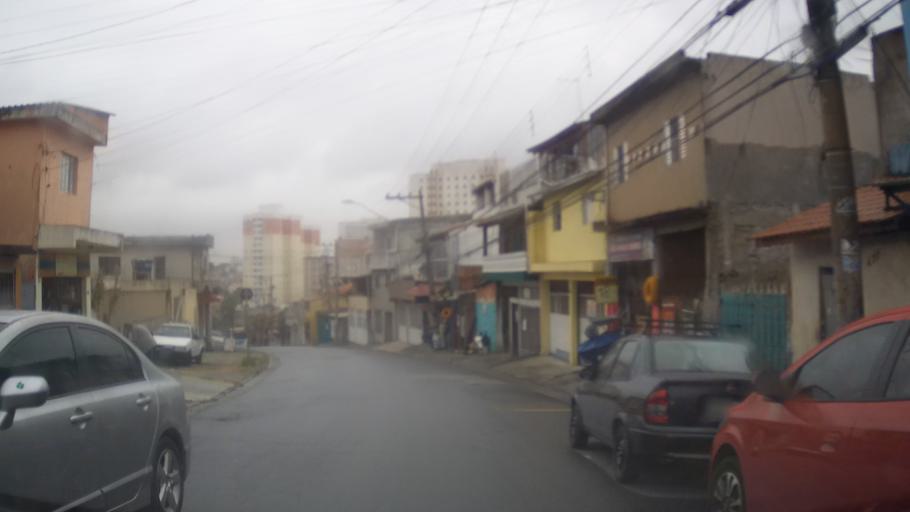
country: BR
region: Sao Paulo
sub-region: Guarulhos
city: Guarulhos
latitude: -23.4423
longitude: -46.5318
